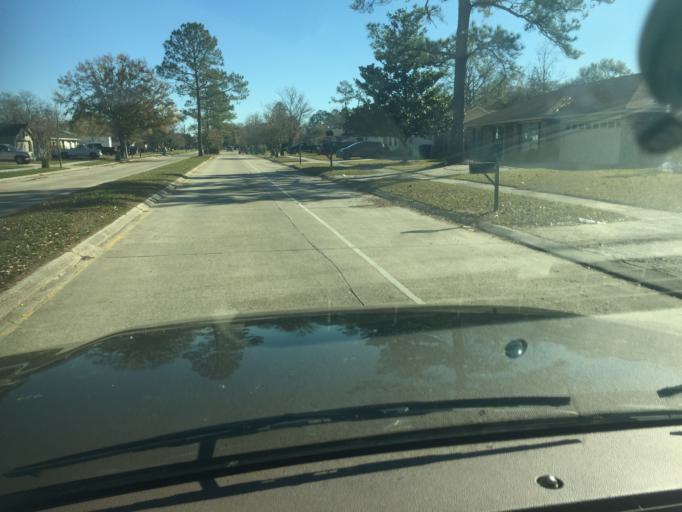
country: US
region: Louisiana
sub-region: Saint Tammany Parish
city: Slidell
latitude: 30.2998
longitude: -89.7654
